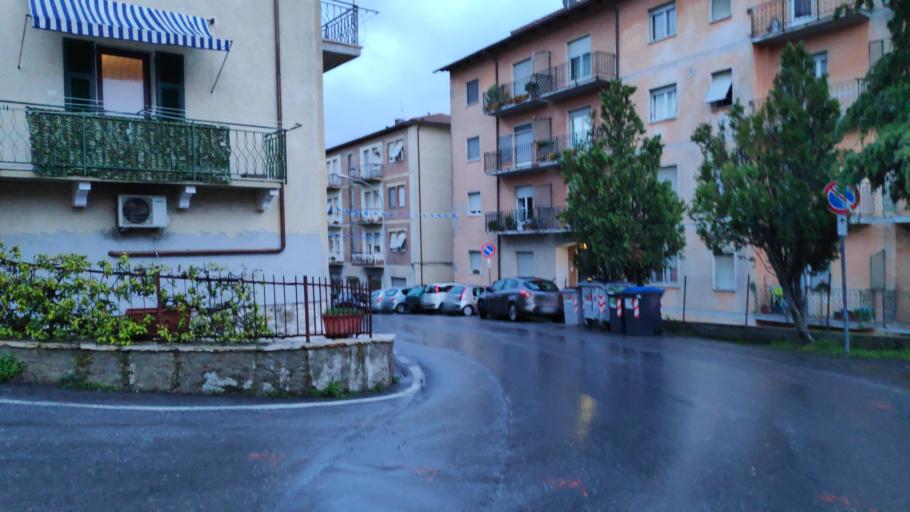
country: IT
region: Tuscany
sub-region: Provincia di Grosseto
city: Manciano
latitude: 42.6207
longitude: 11.4906
